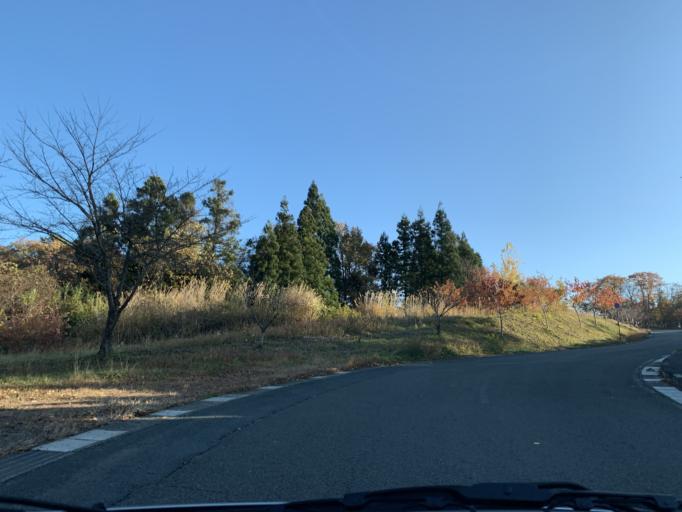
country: JP
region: Iwate
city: Mizusawa
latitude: 39.1950
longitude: 141.1915
